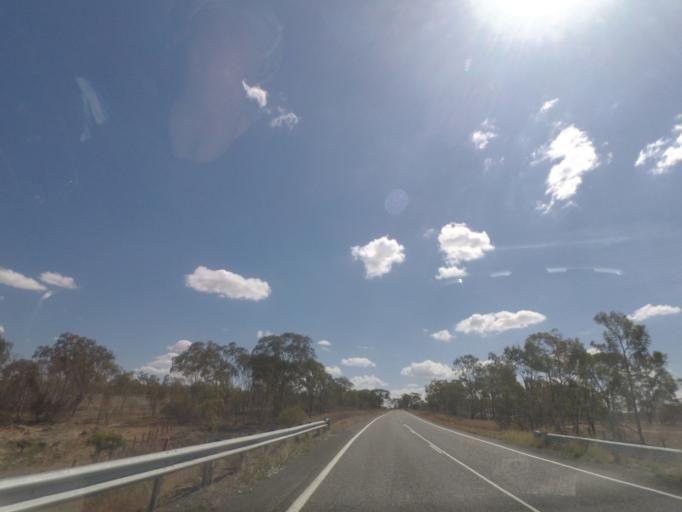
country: AU
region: Queensland
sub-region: Southern Downs
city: Warwick
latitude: -28.2178
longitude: 151.5601
